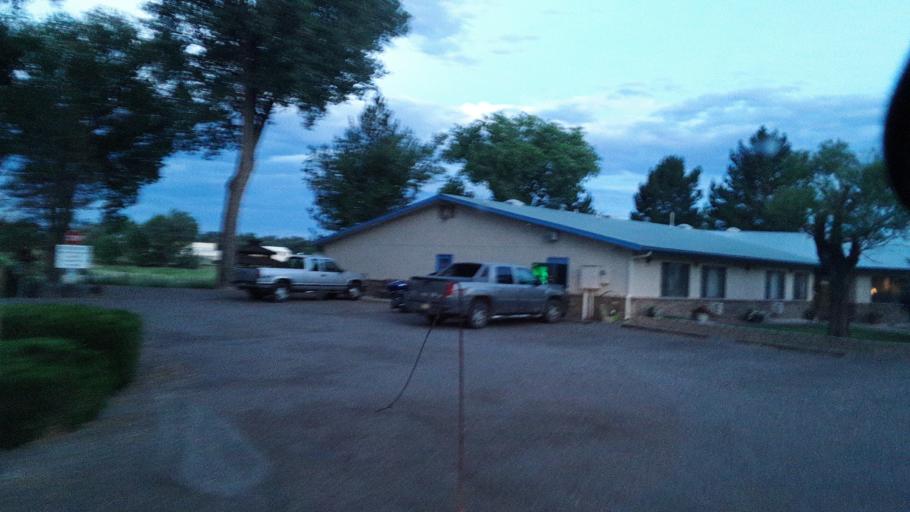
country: US
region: Colorado
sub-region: Delta County
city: Delta
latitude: 38.7524
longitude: -108.0688
